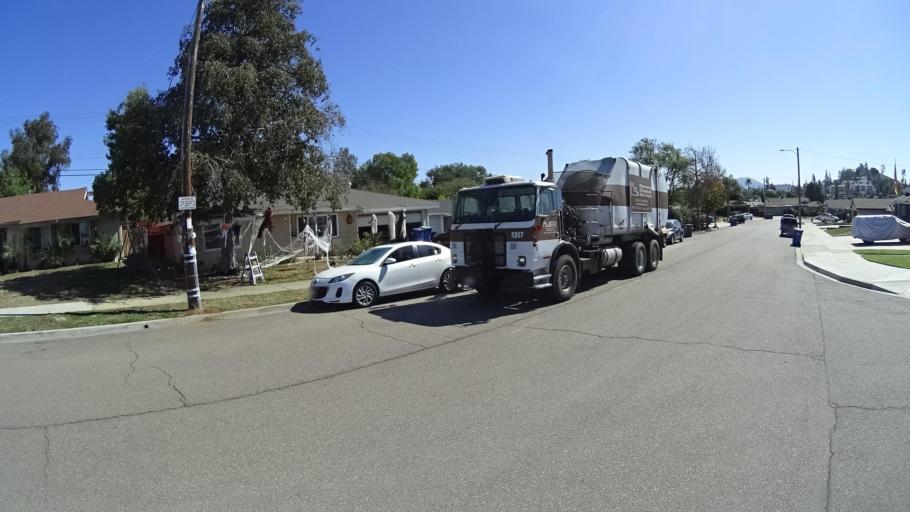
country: US
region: California
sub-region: San Diego County
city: Winter Gardens
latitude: 32.8226
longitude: -116.9523
